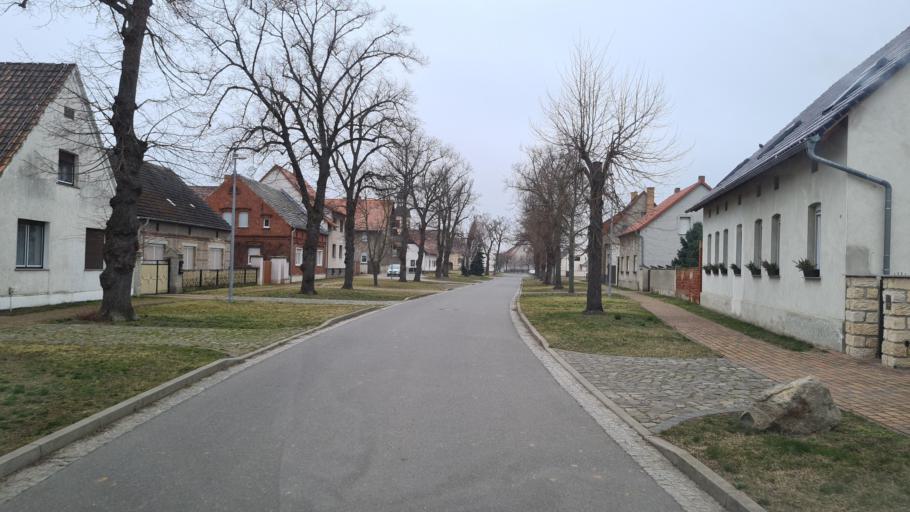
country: DE
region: Brandenburg
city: Herzberg
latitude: 51.6454
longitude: 13.1912
